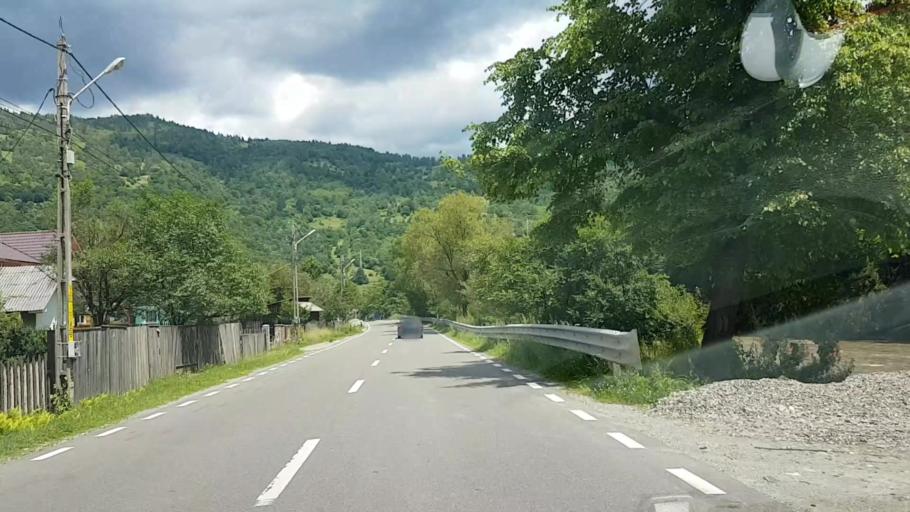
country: RO
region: Suceava
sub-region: Comuna Brosteni
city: Brosteni
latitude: 47.2572
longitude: 25.6782
